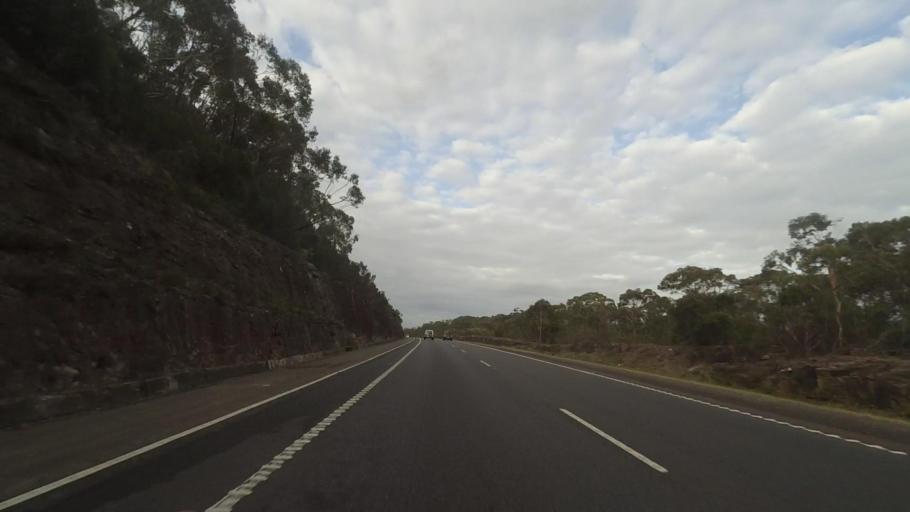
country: AU
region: New South Wales
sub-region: Wollongong
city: Helensburgh
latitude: -34.1775
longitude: 150.9759
